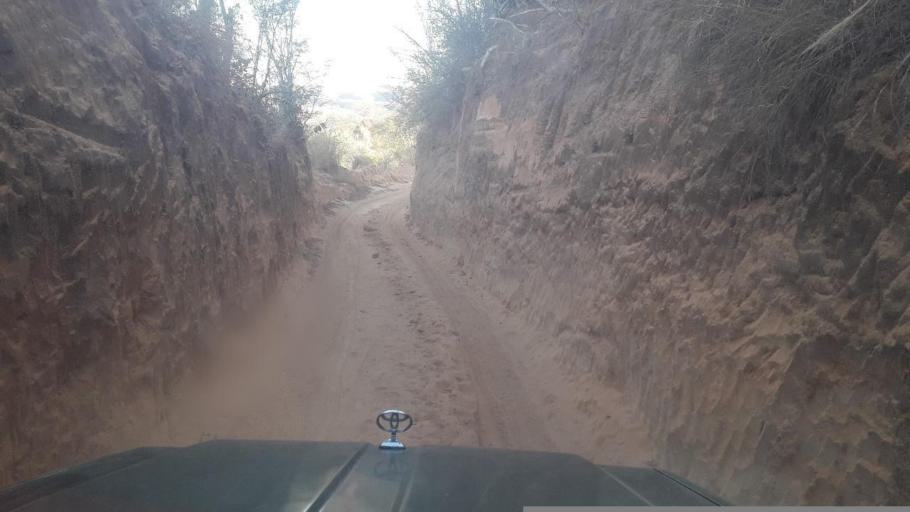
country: MG
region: Boeny
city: Sitampiky
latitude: -16.5036
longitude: 45.6017
